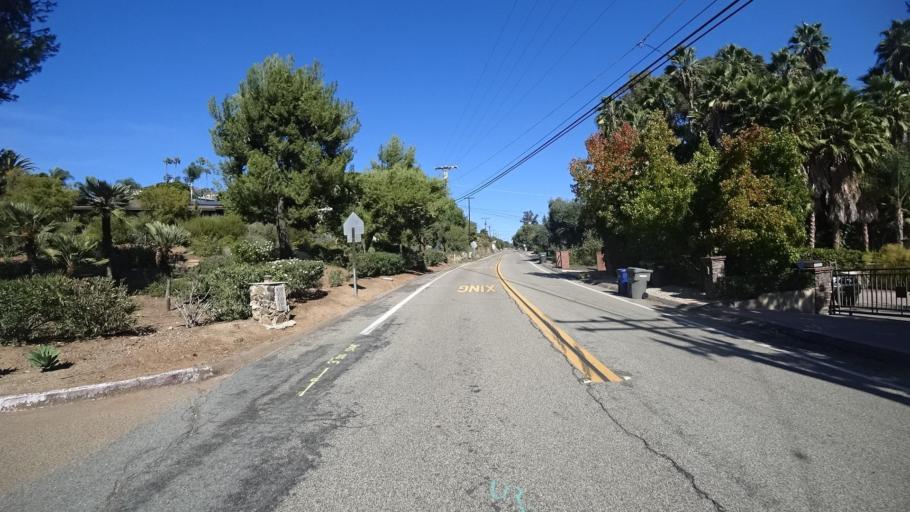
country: US
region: California
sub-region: San Diego County
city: Casa de Oro-Mount Helix
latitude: 32.7594
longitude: -116.9842
